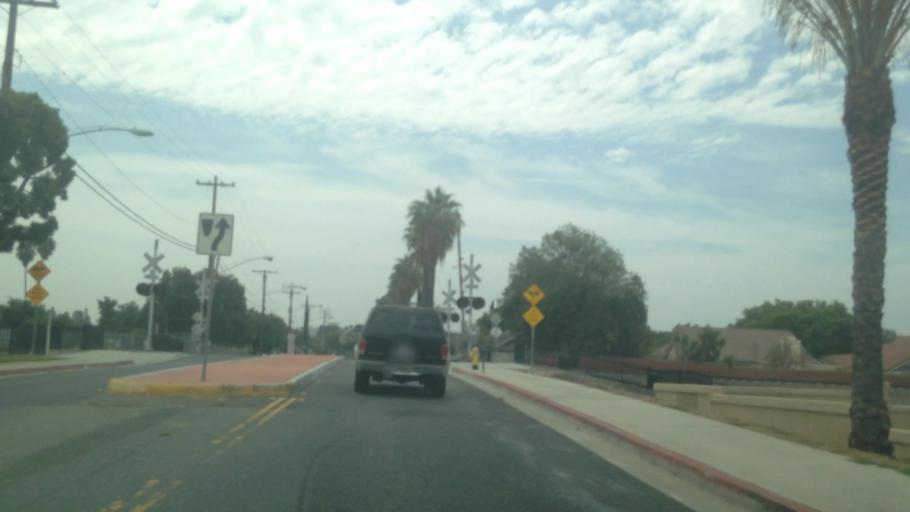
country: US
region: California
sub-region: Riverside County
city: Riverside
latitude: 33.9087
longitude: -117.4479
